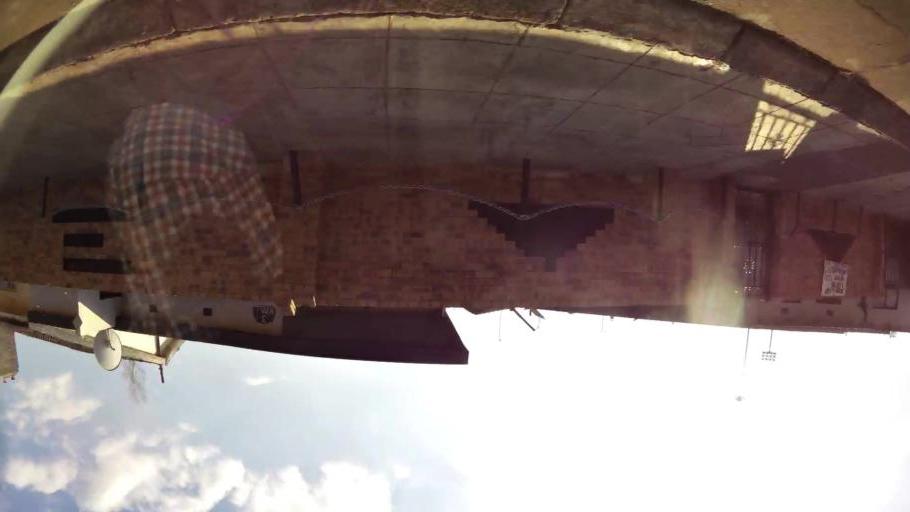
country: ZA
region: Gauteng
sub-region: City of Johannesburg Metropolitan Municipality
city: Soweto
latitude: -26.2591
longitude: 27.9133
